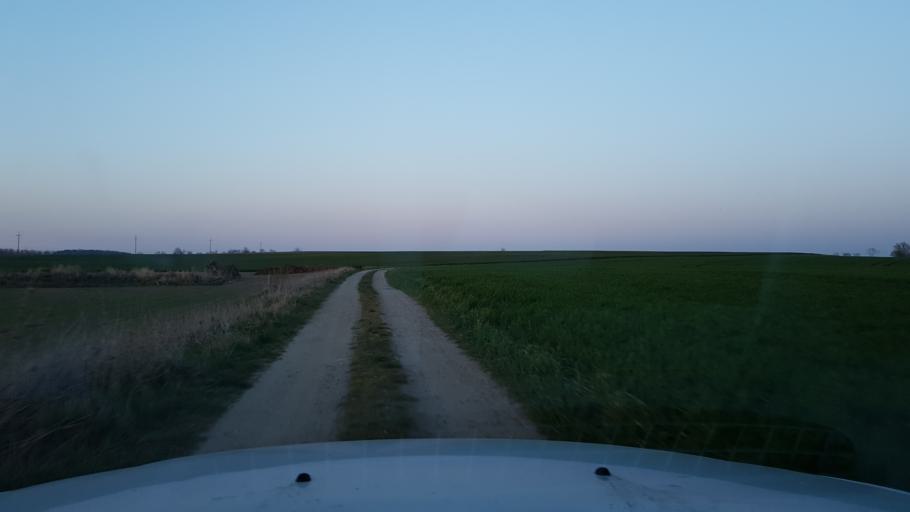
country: PL
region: West Pomeranian Voivodeship
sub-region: Powiat bialogardzki
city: Bialogard
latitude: 53.9611
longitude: 15.9587
